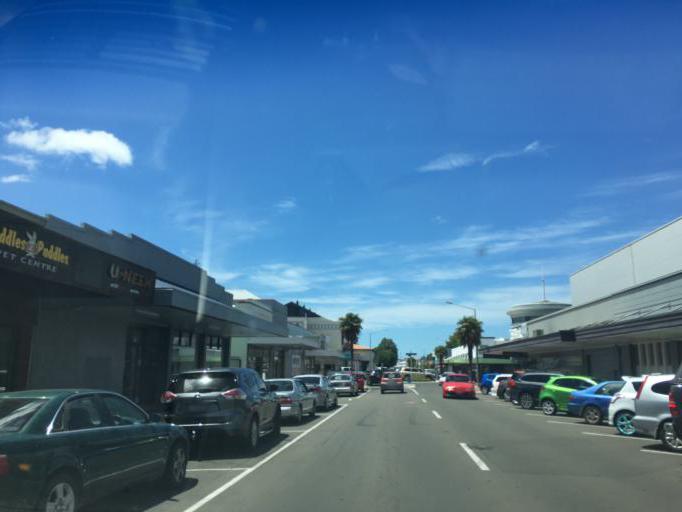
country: NZ
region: Hawke's Bay
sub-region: Hastings District
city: Hastings
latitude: -39.6405
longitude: 176.8407
